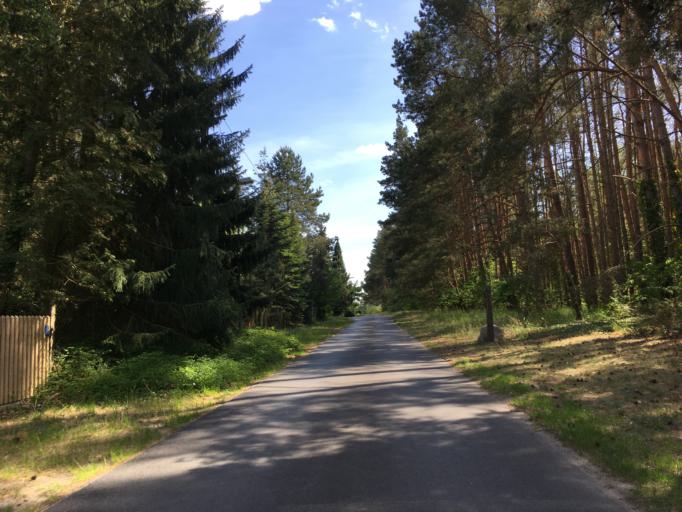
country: DE
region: Brandenburg
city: Oderberg
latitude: 52.8420
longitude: 14.1169
